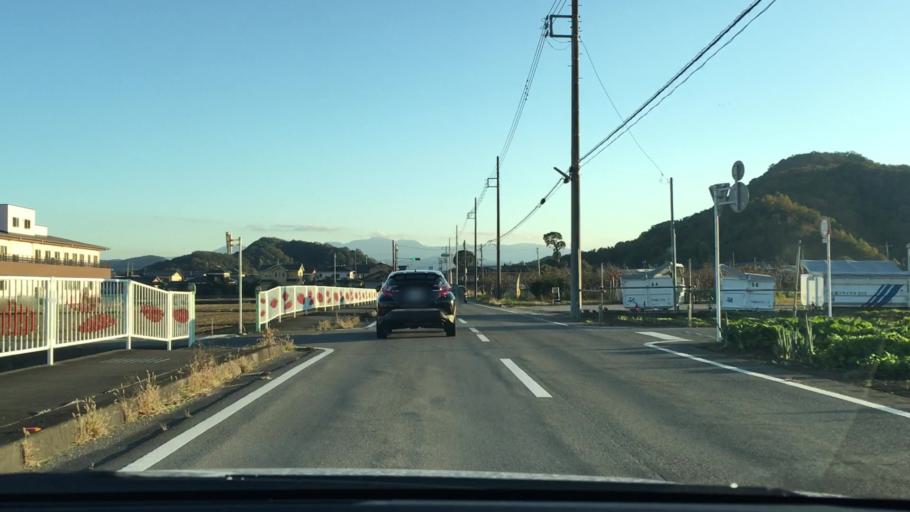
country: JP
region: Shizuoka
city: Mishima
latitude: 35.0587
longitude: 138.9313
